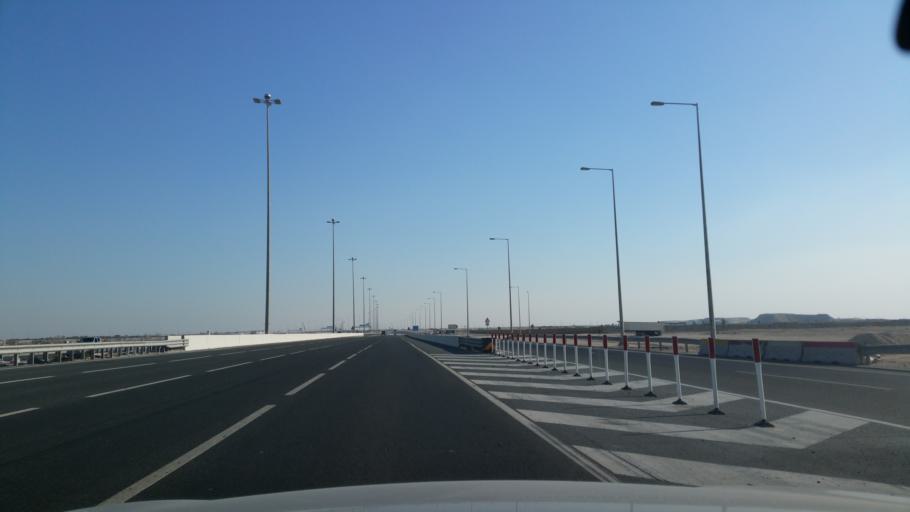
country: QA
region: Al Wakrah
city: Al Wukayr
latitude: 25.1528
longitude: 51.4737
